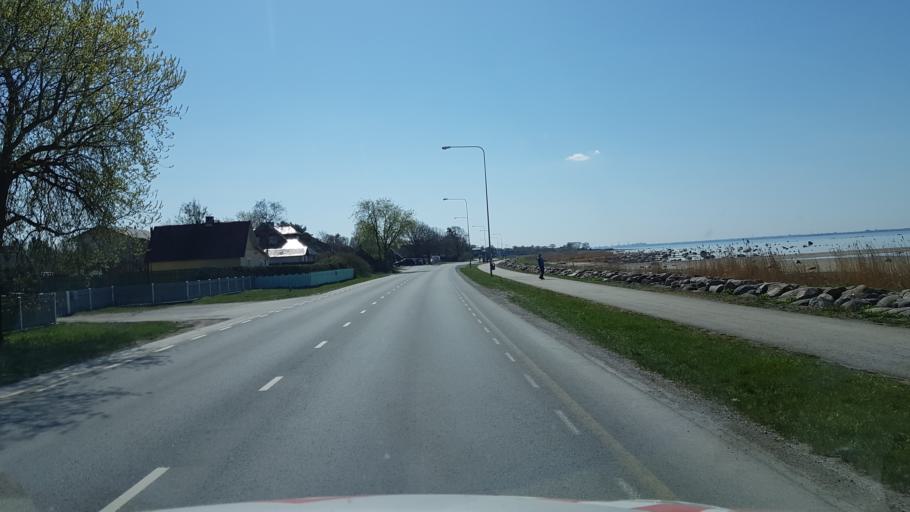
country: EE
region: Harju
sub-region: Viimsi vald
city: Rummu
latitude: 59.5521
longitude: 24.7951
